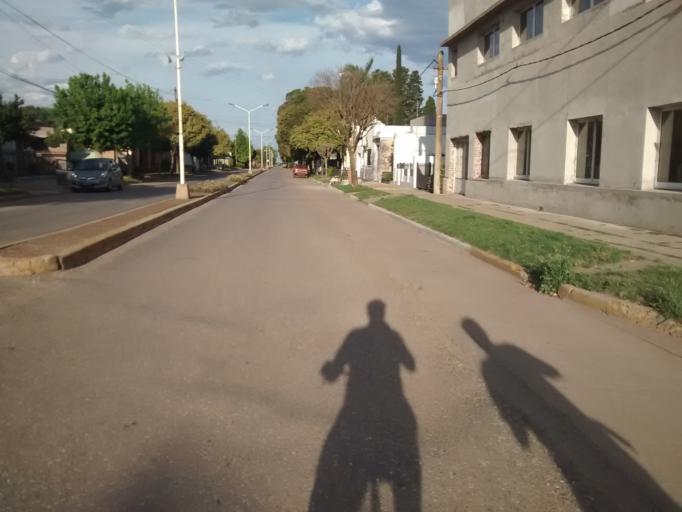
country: AR
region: Santa Fe
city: Galvez
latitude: -31.9044
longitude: -61.2776
